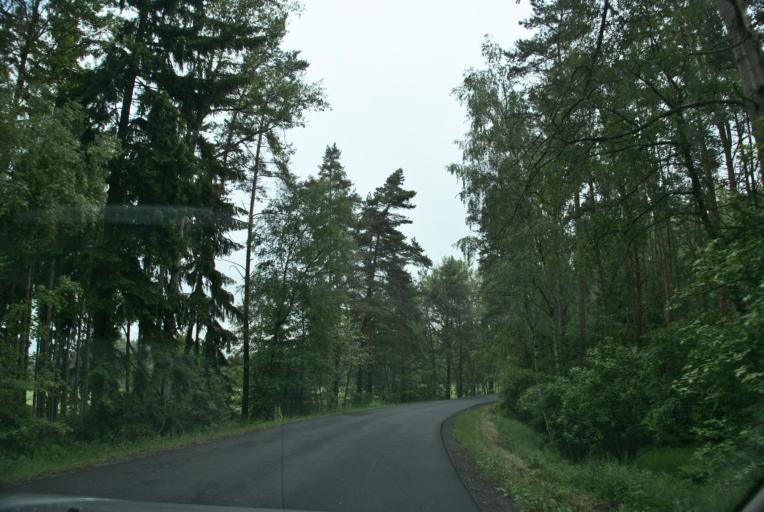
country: CZ
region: Plzensky
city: Zihle
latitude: 50.0301
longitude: 13.3961
